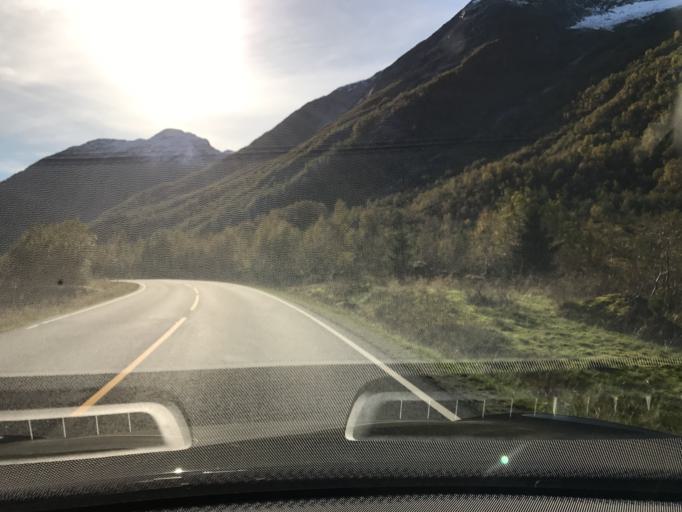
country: NO
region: Sogn og Fjordane
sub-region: Jolster
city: Skei
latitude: 61.4740
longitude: 6.7412
